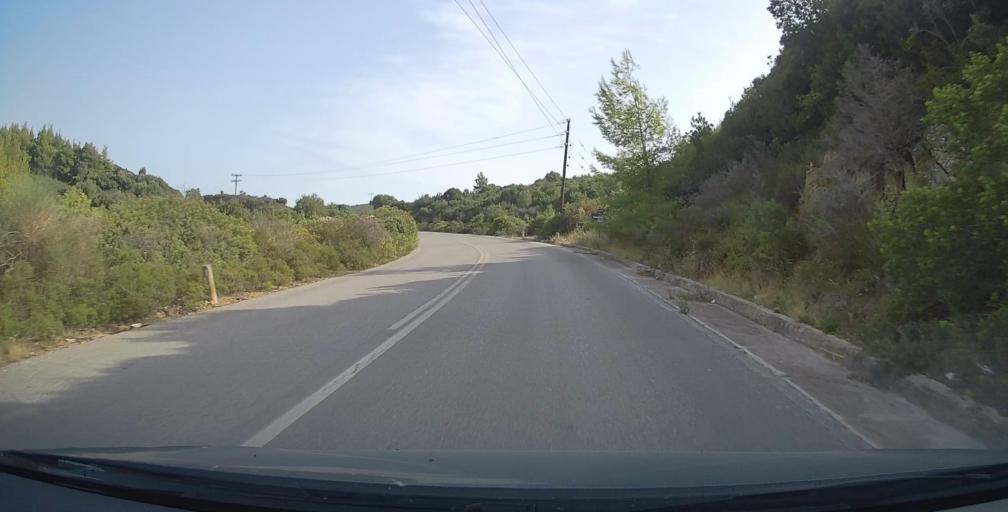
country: GR
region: Central Macedonia
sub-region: Nomos Chalkidikis
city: Sykia
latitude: 39.9620
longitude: 23.9475
